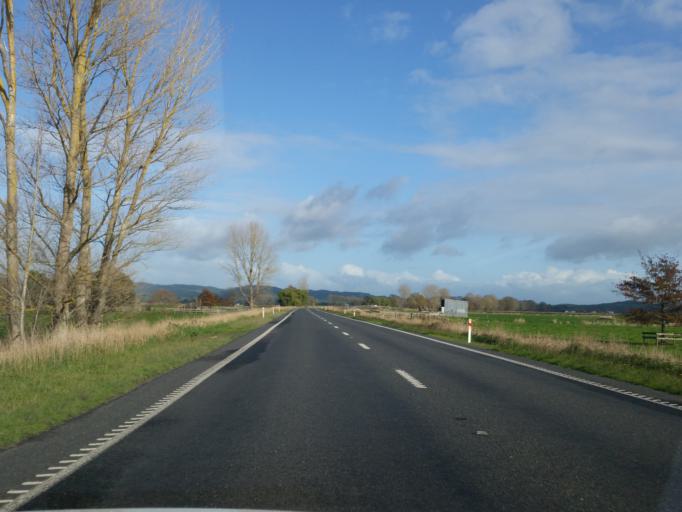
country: NZ
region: Waikato
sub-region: Hauraki District
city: Ngatea
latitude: -37.2768
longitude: 175.4622
